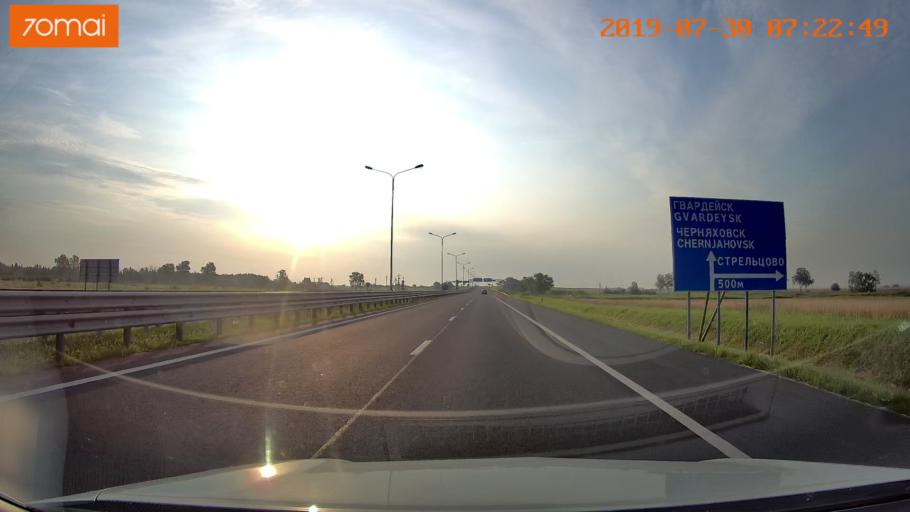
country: RU
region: Kaliningrad
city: Bol'shoe Isakovo
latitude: 54.6921
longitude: 20.7662
